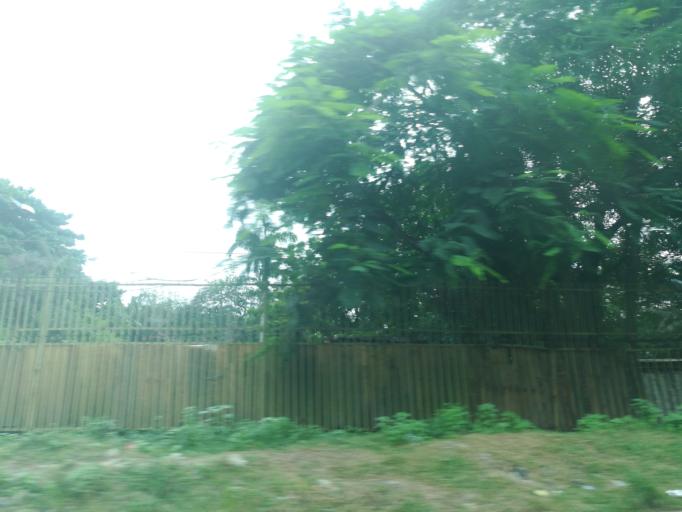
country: NG
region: Lagos
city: Lagos
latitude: 6.4377
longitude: 3.4088
